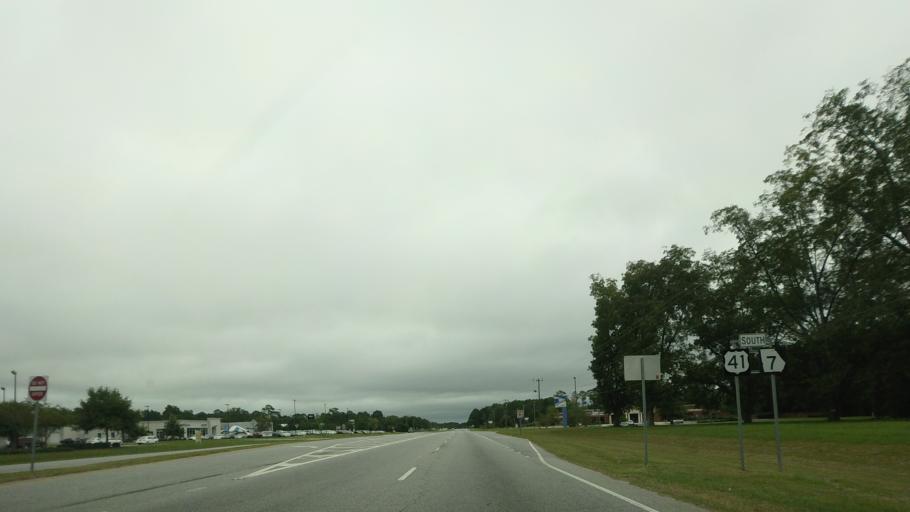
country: US
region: Georgia
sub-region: Lowndes County
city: Valdosta
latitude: 30.8827
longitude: -83.2718
